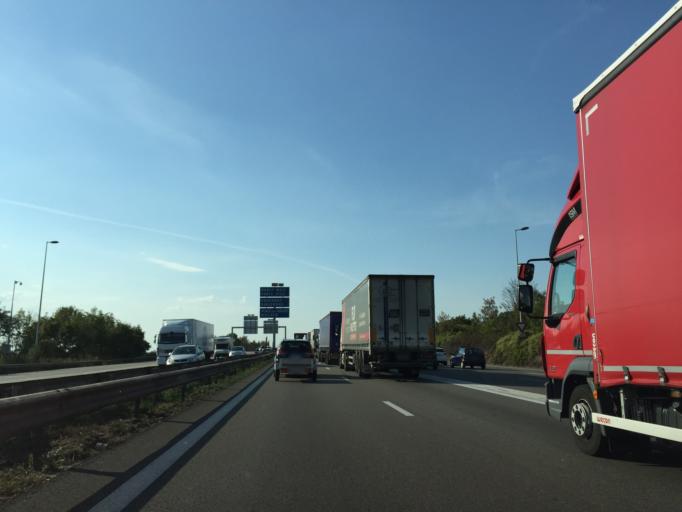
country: FR
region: Alsace
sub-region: Departement du Bas-Rhin
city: Strasbourg
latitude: 48.5757
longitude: 7.7282
